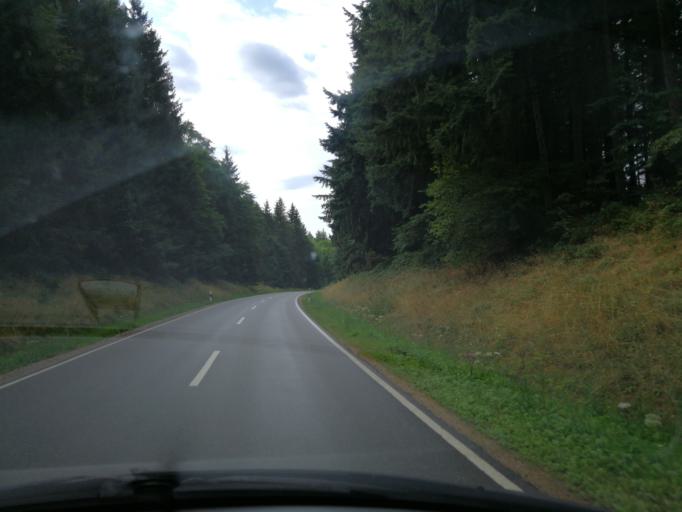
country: DE
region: Bavaria
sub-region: Upper Palatinate
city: Wiesent
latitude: 49.0281
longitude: 12.3737
